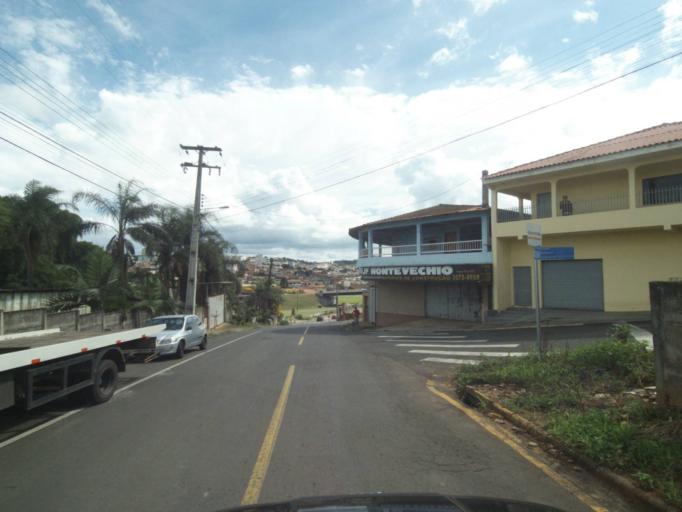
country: BR
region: Parana
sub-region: Telemaco Borba
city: Telemaco Borba
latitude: -24.3236
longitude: -50.6266
